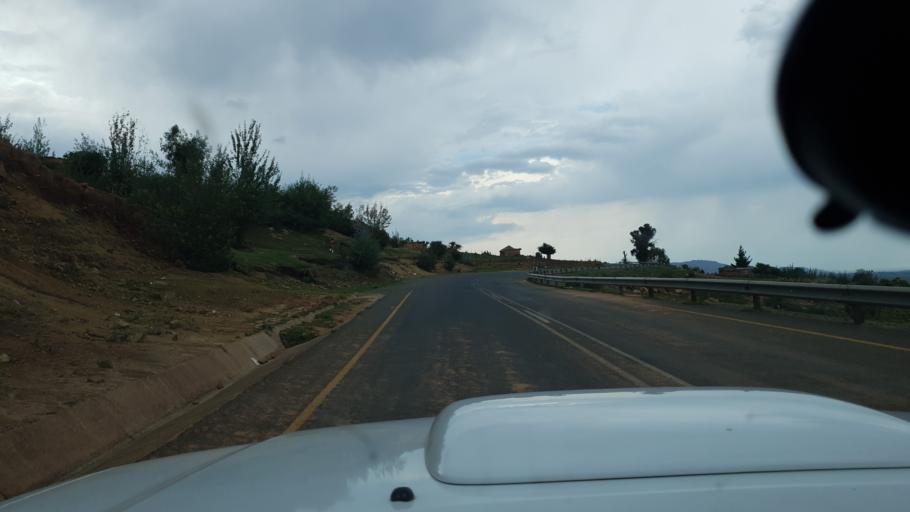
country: LS
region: Maseru
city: Maseru
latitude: -29.4605
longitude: 27.4909
